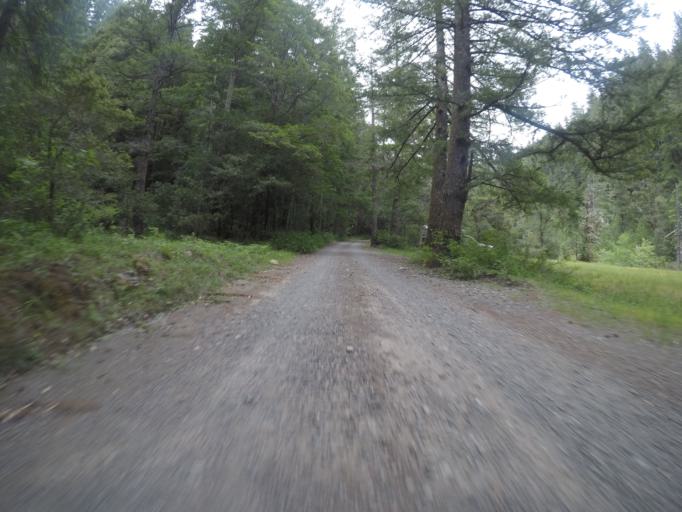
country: US
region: California
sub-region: Del Norte County
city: Bertsch-Oceanview
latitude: 41.7321
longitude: -123.8860
